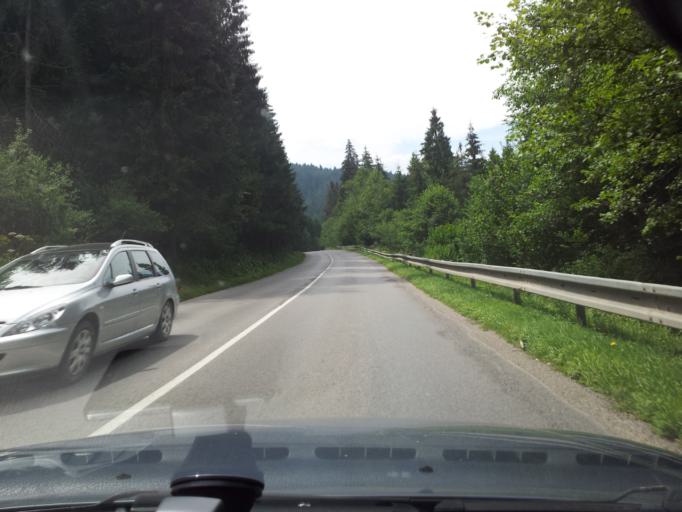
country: SK
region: Zilinsky
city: Oravska Lesna
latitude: 49.3801
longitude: 19.3232
